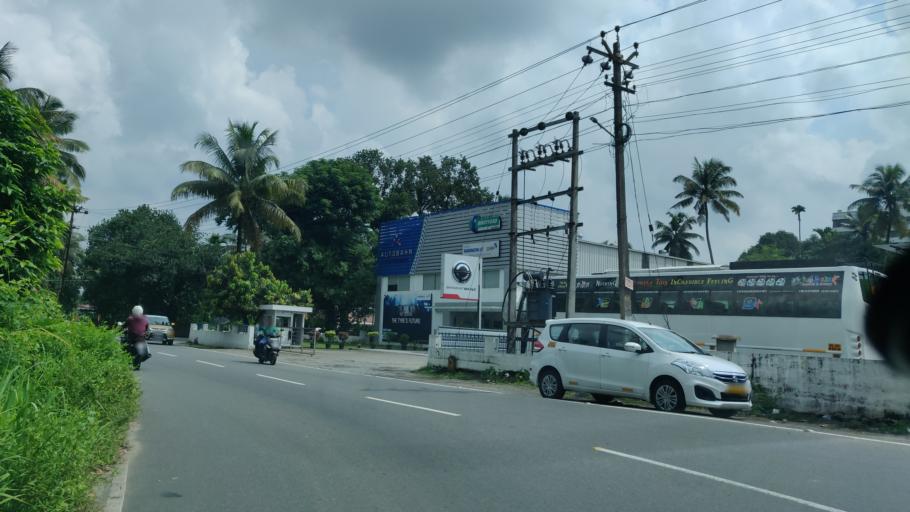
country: IN
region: Kerala
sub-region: Ernakulam
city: Angamali
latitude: 10.1693
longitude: 76.4244
